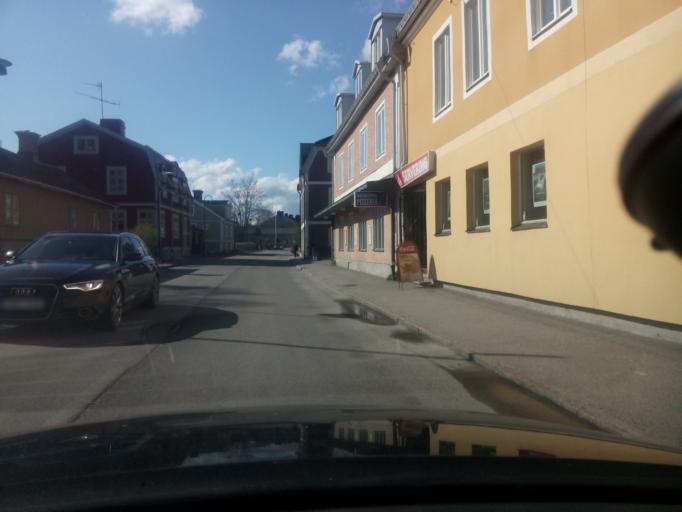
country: SE
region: Soedermanland
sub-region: Flens Kommun
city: Malmkoping
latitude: 59.1319
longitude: 16.7307
